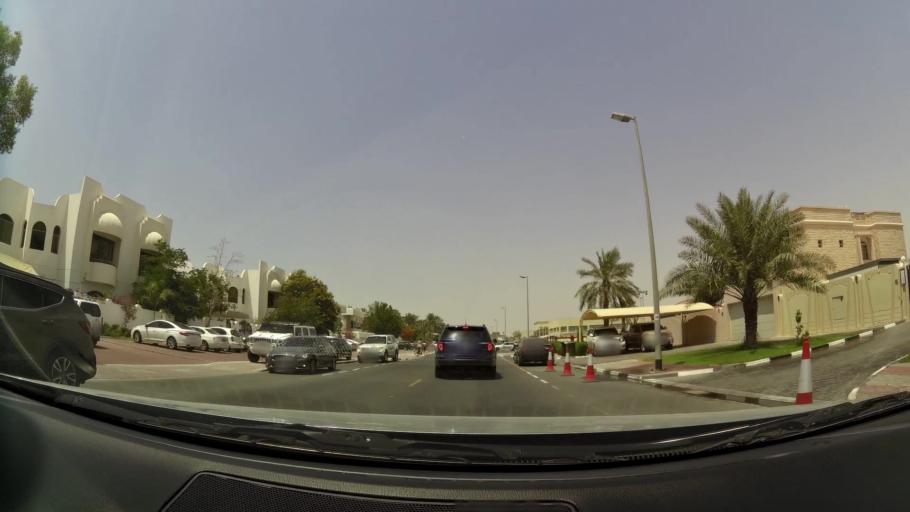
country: AE
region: Dubai
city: Dubai
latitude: 25.1395
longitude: 55.1946
